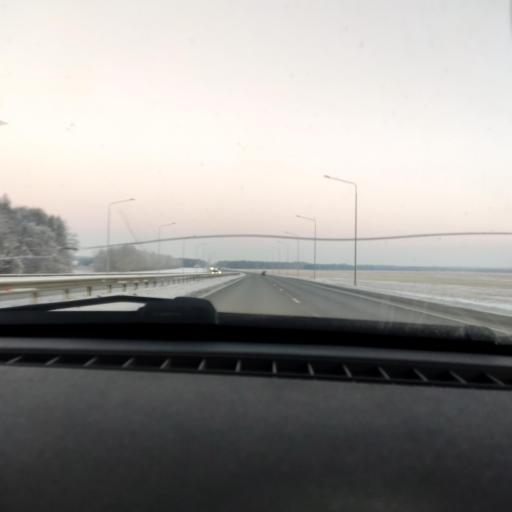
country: RU
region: Bashkortostan
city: Kabakovo
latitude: 54.4374
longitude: 55.9225
